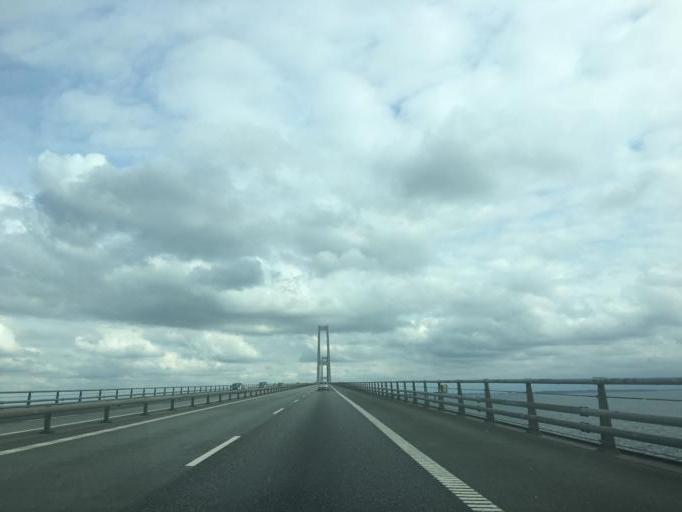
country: DK
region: Zealand
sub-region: Slagelse Kommune
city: Korsor
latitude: 55.3362
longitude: 10.9933
